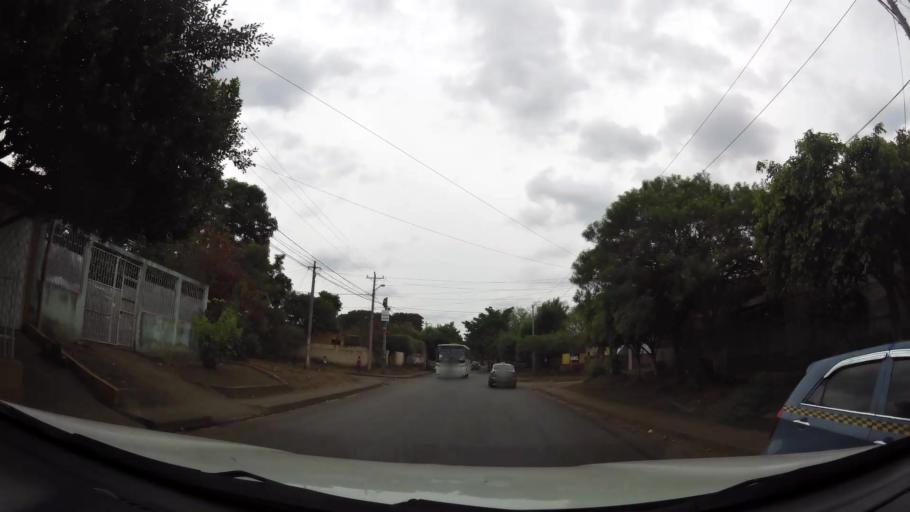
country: NI
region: Managua
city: Managua
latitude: 12.1202
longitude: -86.1956
